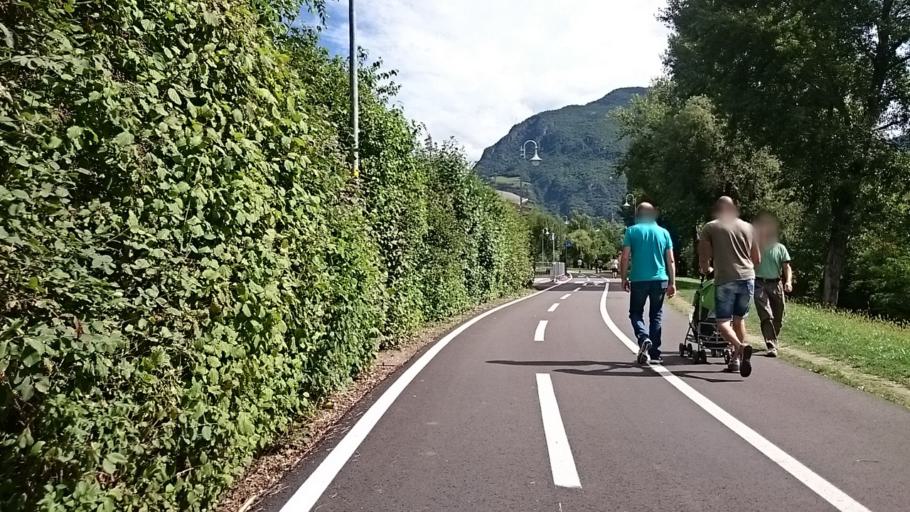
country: IT
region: Trentino-Alto Adige
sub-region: Bolzano
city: Bolzano
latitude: 46.4911
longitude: 11.3462
